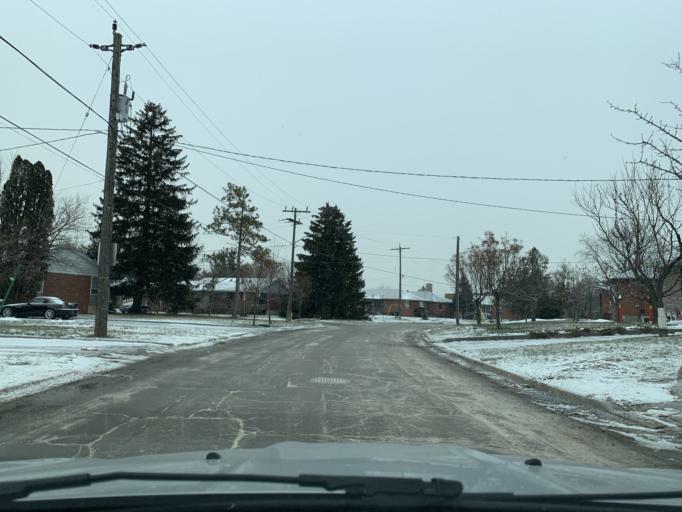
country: CA
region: Ontario
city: Concord
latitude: 43.7370
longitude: -79.4904
